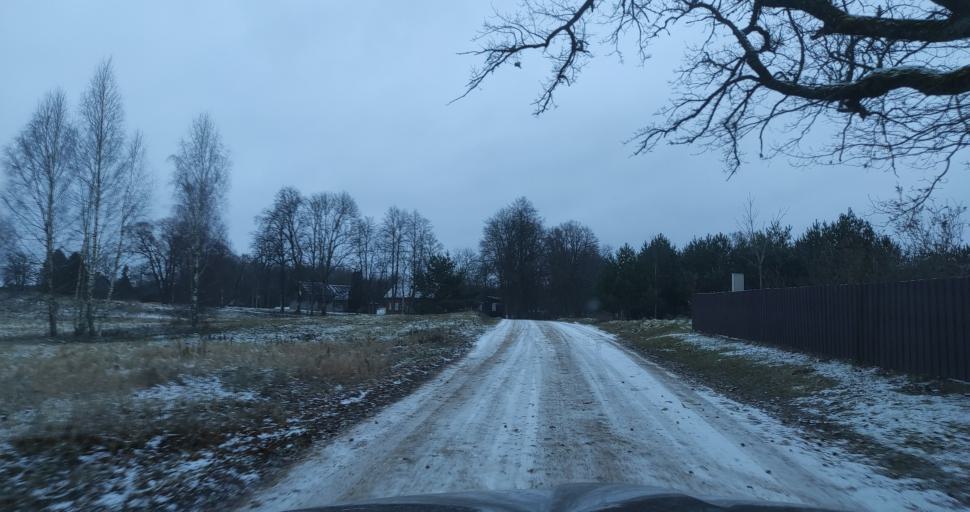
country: LV
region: Kuldigas Rajons
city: Kuldiga
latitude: 56.9791
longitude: 22.0522
